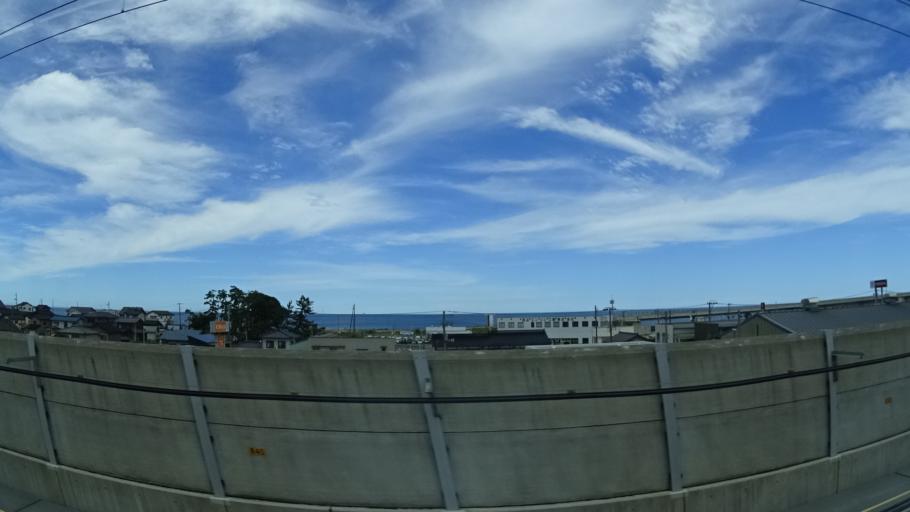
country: JP
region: Niigata
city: Itoigawa
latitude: 37.0465
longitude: 137.8725
